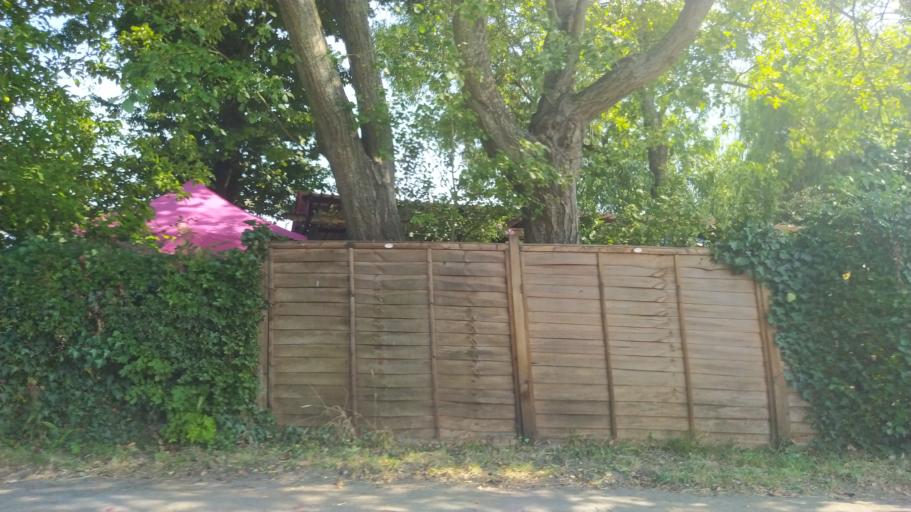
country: GB
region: England
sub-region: Hampshire
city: Cadnam
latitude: 50.9283
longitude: -1.5488
